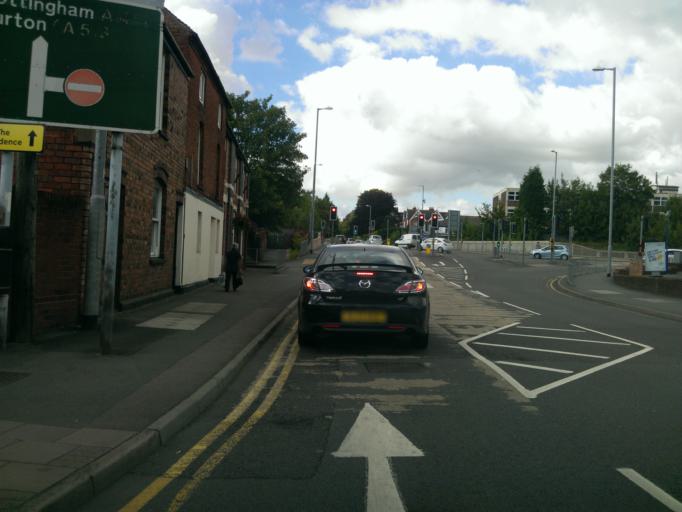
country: GB
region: England
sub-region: Staffordshire
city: Tamworth
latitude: 52.6370
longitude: -1.6946
